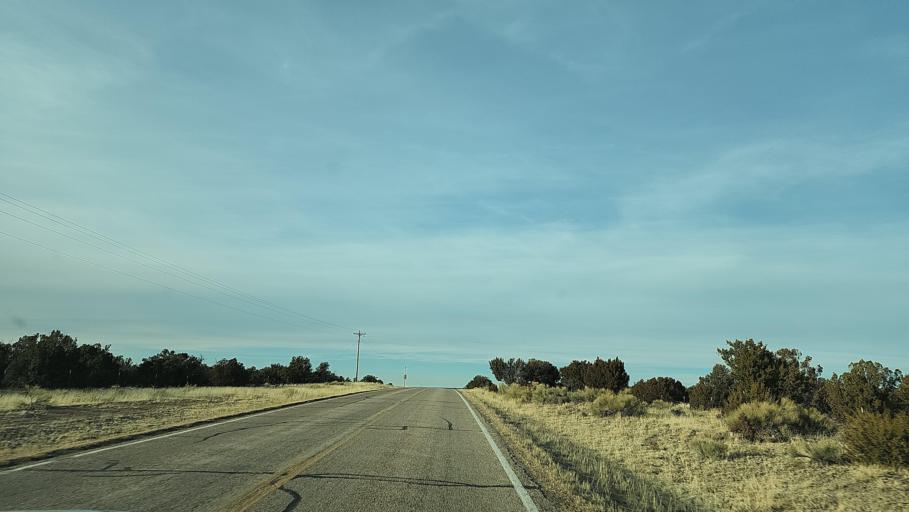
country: US
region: New Mexico
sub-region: McKinley County
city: Black Rock
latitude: 34.4345
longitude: -108.4276
